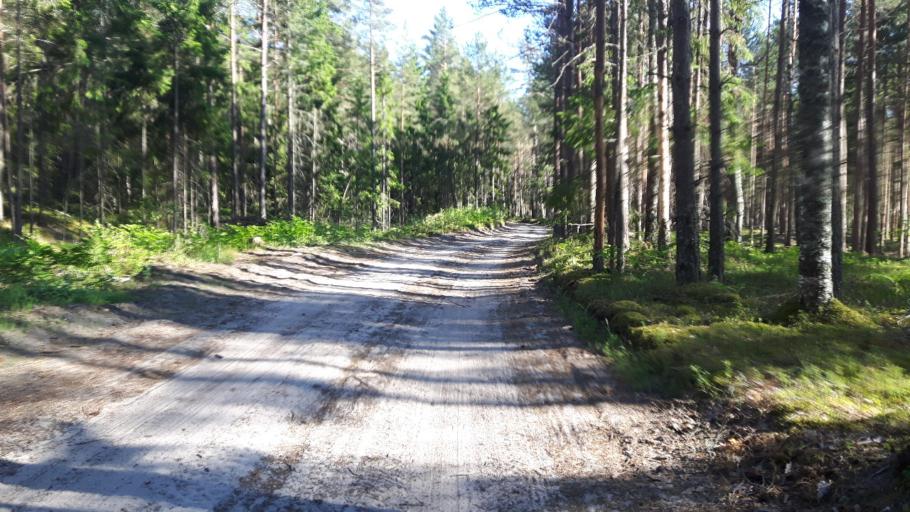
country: LV
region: Salacgrivas
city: Salacgriva
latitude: 57.7170
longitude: 24.3483
